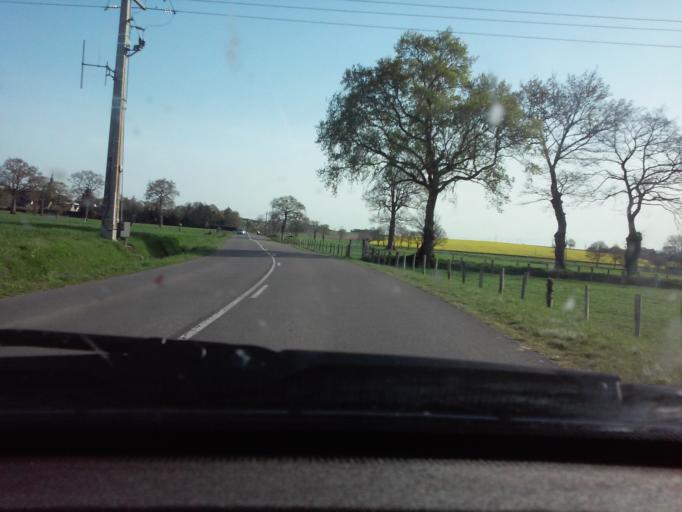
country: FR
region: Brittany
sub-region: Departement d'Ille-et-Vilaine
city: Javene
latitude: 48.3281
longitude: -1.2202
